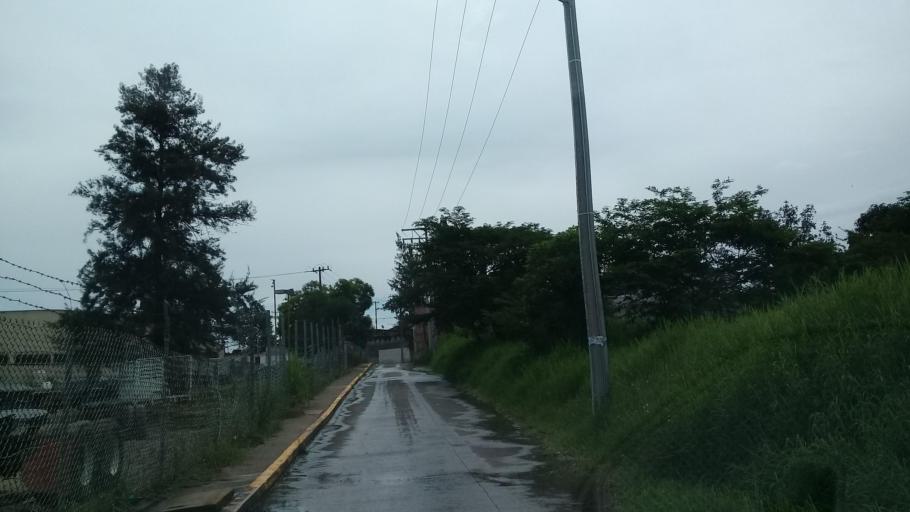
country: MX
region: Veracruz
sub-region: Emiliano Zapata
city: Dos Rios
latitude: 19.4818
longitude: -96.7995
